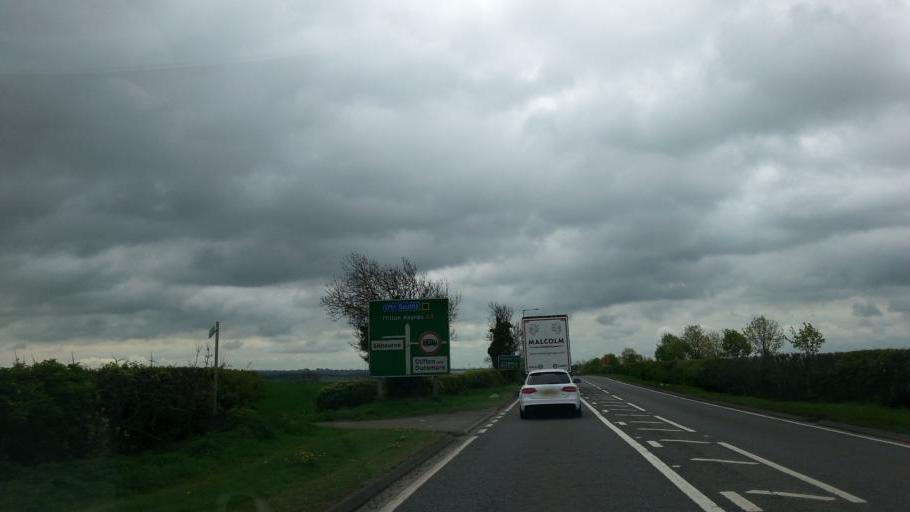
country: GB
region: England
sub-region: Leicestershire
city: Lutterworth
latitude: 52.3884
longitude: -1.1954
